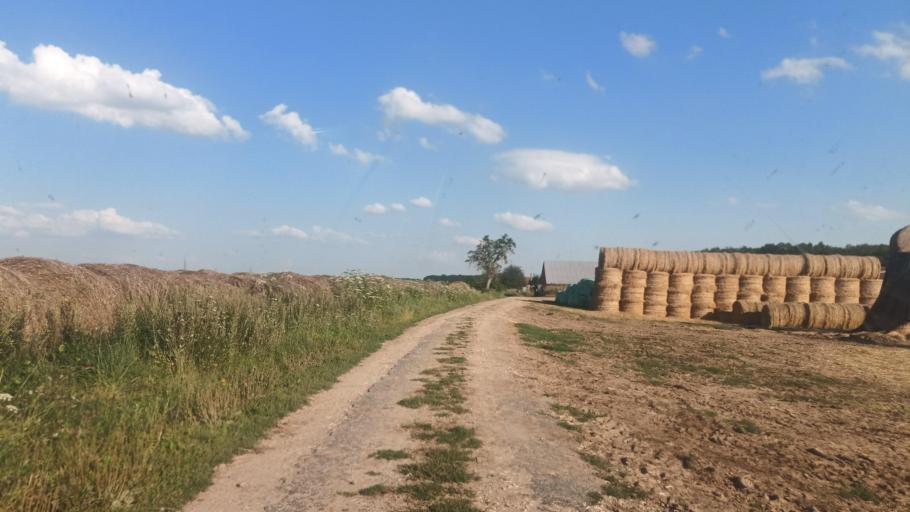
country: FR
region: Bourgogne
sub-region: Departement de l'Yonne
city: Saint-Valerien
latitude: 48.2236
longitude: 3.0836
